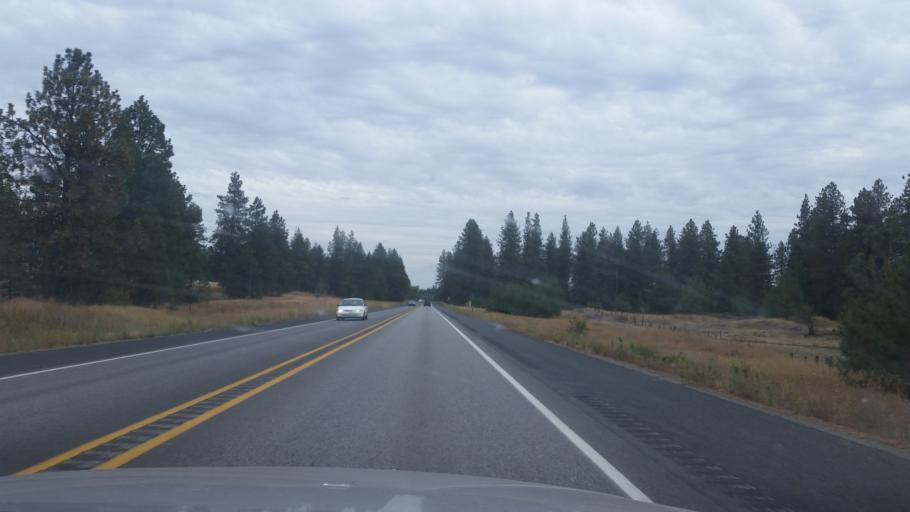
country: US
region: Washington
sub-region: Spokane County
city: Cheney
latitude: 47.5381
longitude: -117.5777
